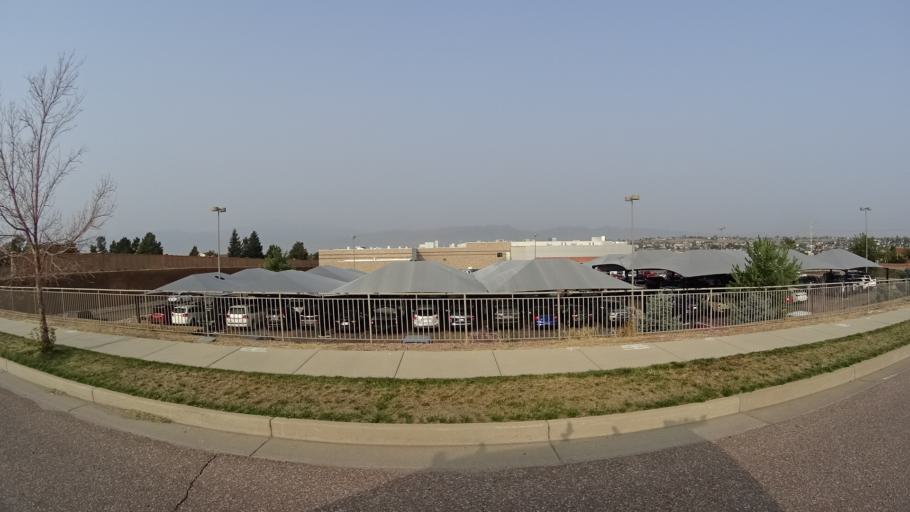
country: US
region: Colorado
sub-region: El Paso County
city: Black Forest
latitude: 38.9380
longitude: -104.7295
